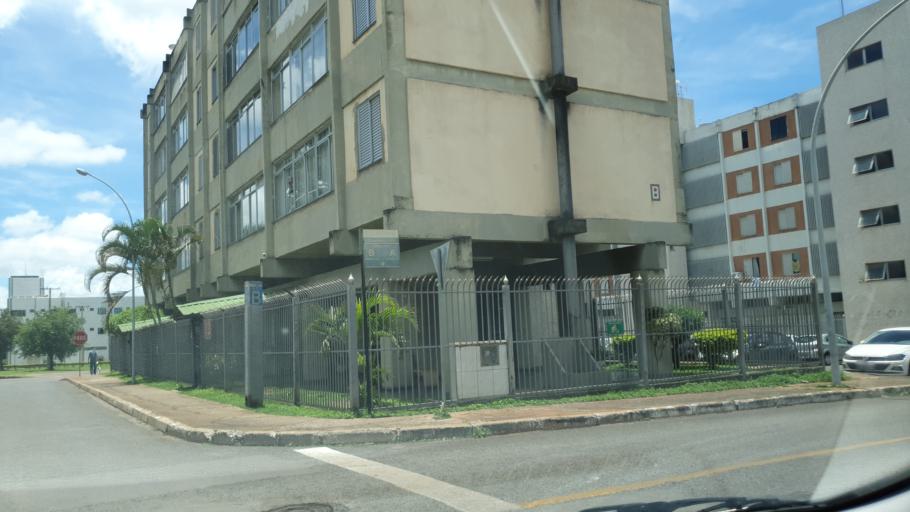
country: BR
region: Federal District
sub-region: Brasilia
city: Brasilia
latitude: -15.7985
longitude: -47.9379
